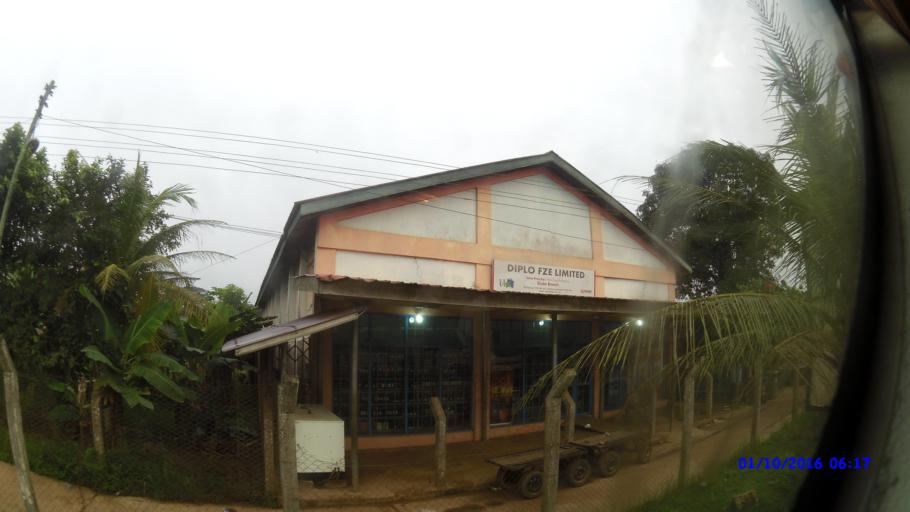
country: CI
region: Sud-Comoe
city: Mafere
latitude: 5.2893
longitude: -2.7804
